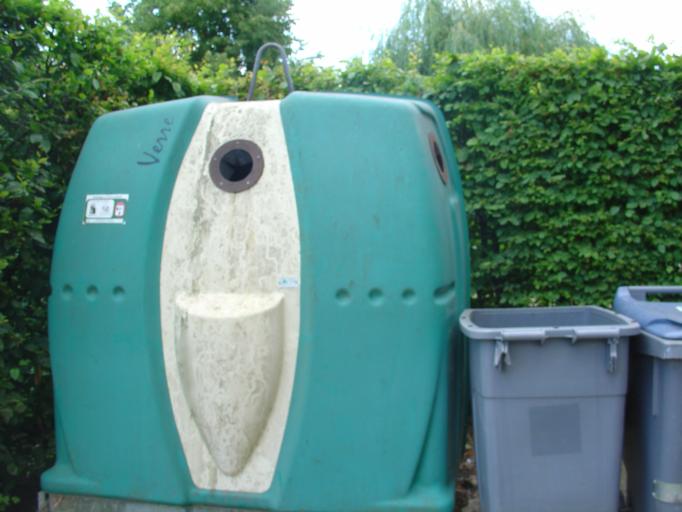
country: FR
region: Lorraine
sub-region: Departement de la Meuse
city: Dieue-sur-Meuse
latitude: 48.9398
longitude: 5.4097
